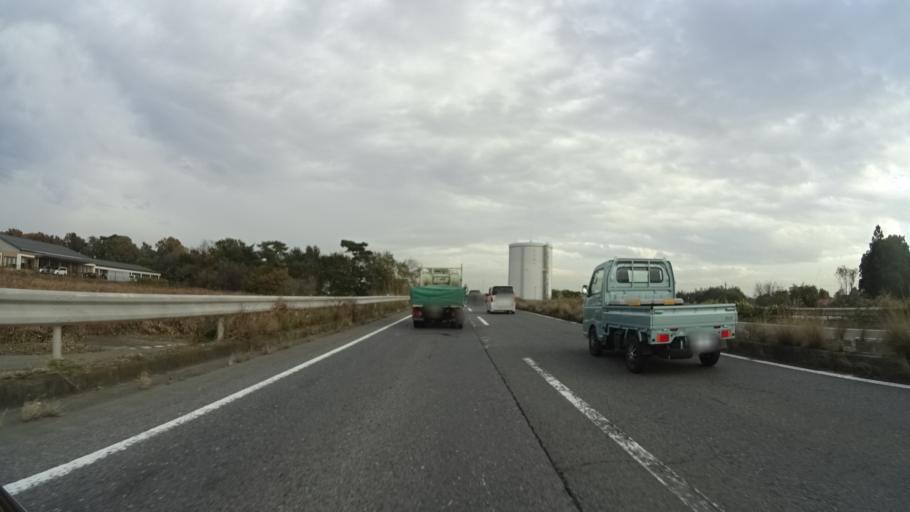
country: JP
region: Gunma
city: Isesaki
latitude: 36.3623
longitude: 139.1896
